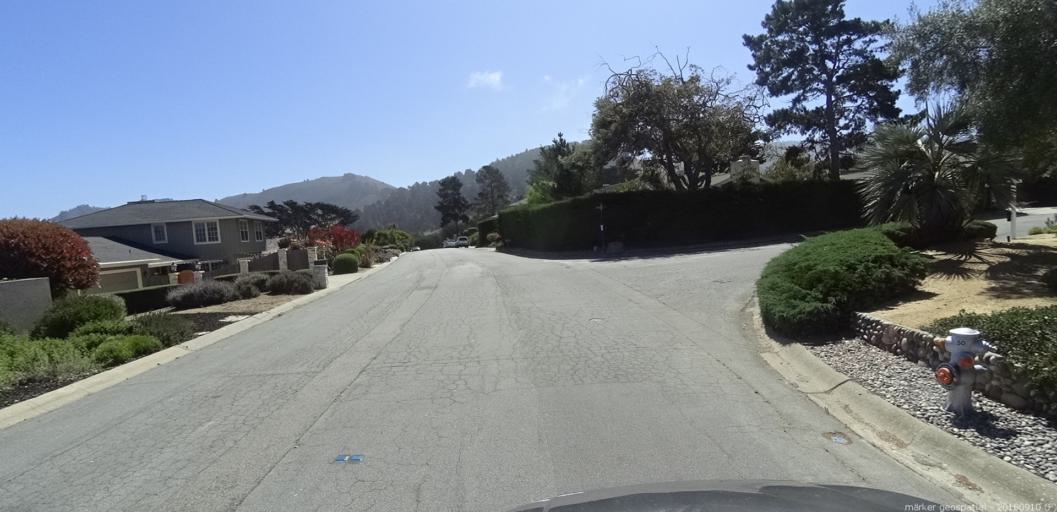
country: US
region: California
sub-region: Monterey County
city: Carmel-by-the-Sea
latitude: 36.5323
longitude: -121.9231
